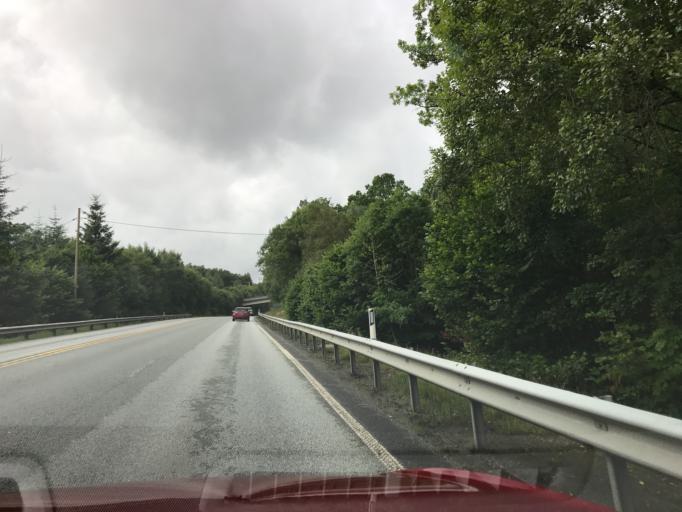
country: NO
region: Rogaland
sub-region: Tysvaer
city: Aksdal
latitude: 59.4208
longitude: 5.4172
